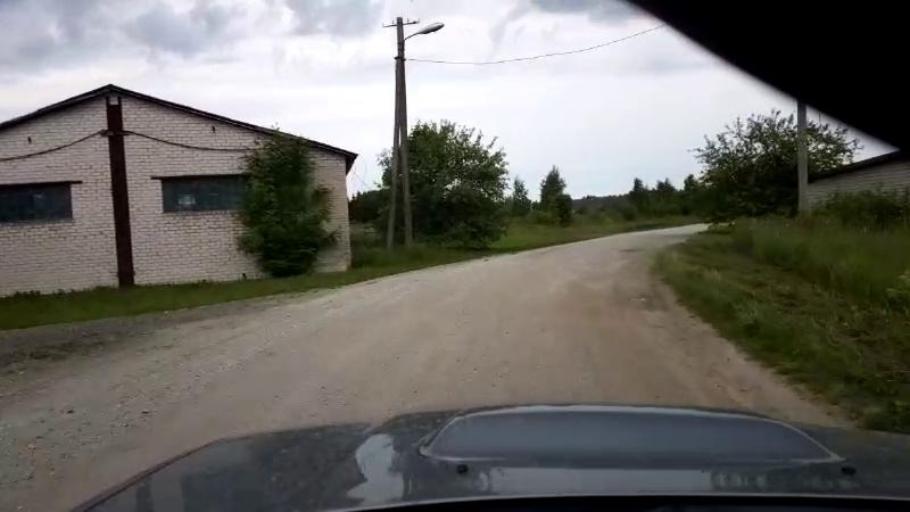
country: EE
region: Paernumaa
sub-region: Tootsi vald
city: Tootsi
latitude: 58.5313
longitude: 24.7037
